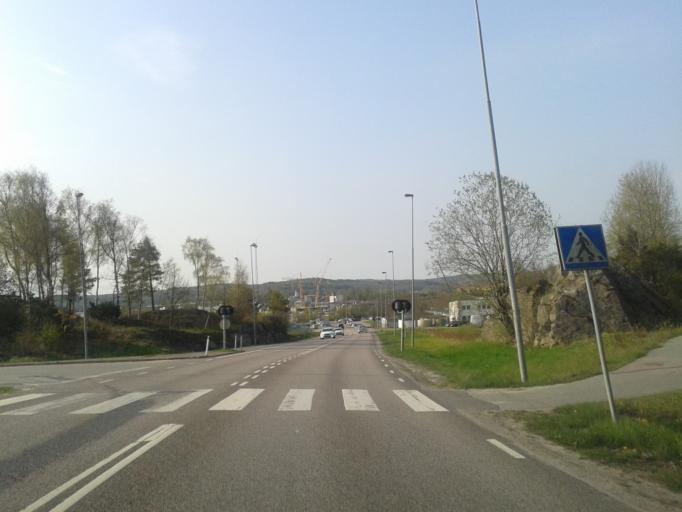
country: SE
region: Vaestra Goetaland
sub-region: Kungalvs Kommun
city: Kungalv
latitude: 57.8806
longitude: 11.9718
